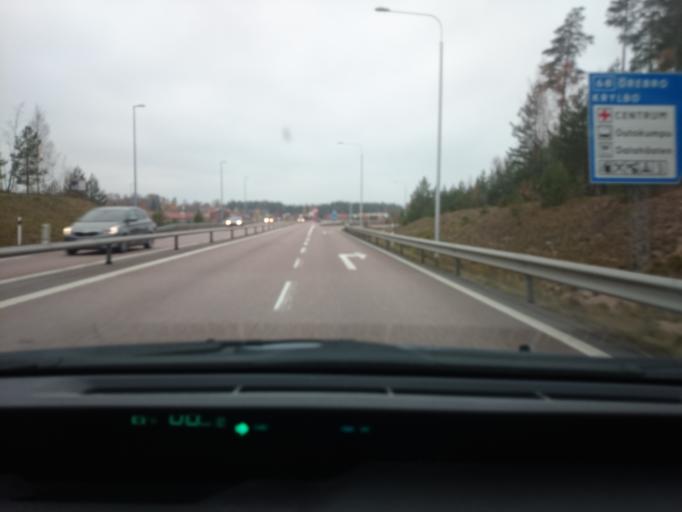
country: SE
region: Dalarna
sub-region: Avesta Kommun
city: Avesta
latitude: 60.1518
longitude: 16.2086
